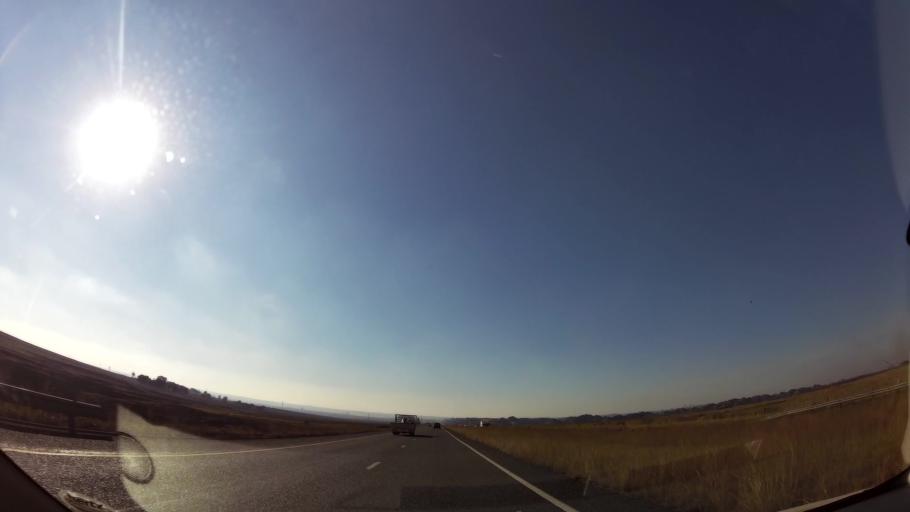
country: ZA
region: Mpumalanga
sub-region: Nkangala District Municipality
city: Witbank
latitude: -26.0195
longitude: 28.9984
